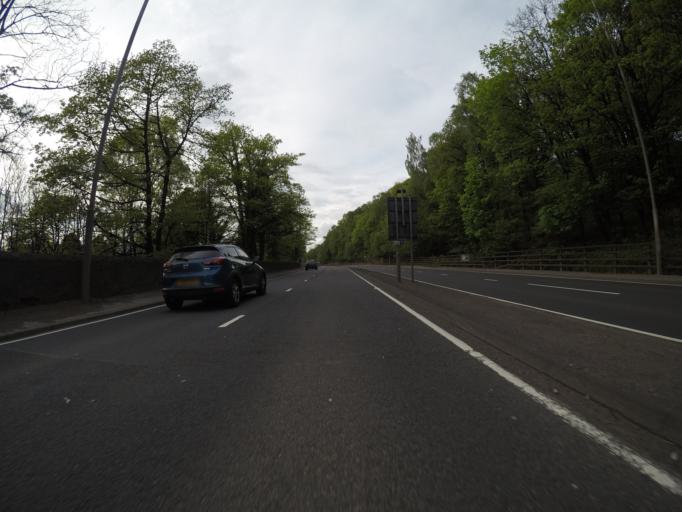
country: GB
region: Scotland
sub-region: West Dunbartonshire
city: Dumbarton
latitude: 55.9387
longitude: -4.5358
